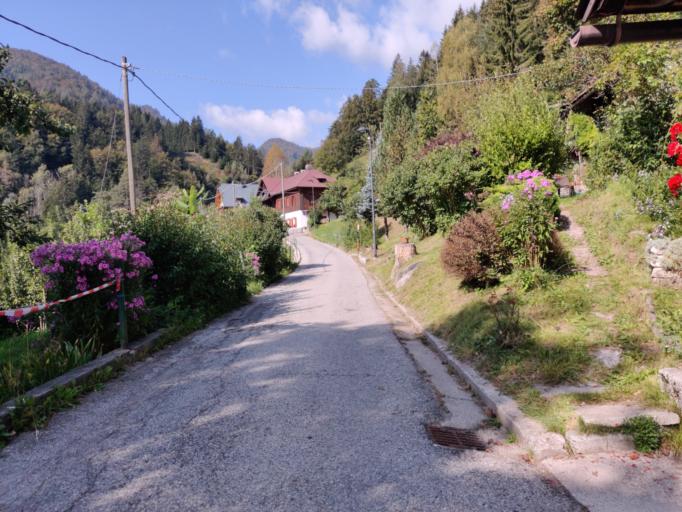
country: IT
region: Friuli Venezia Giulia
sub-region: Provincia di Udine
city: Tarvisio
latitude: 46.5205
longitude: 13.6127
